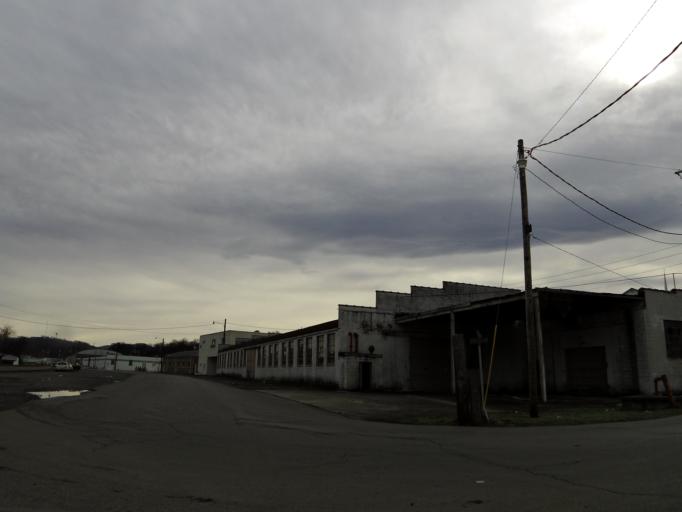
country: US
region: Tennessee
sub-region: Cocke County
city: Newport
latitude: 35.9693
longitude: -83.1962
